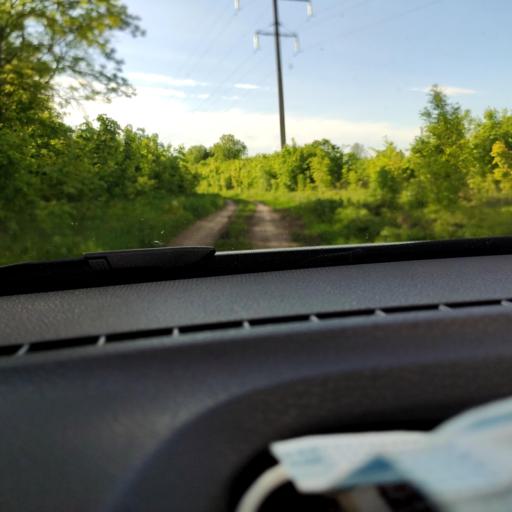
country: RU
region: Voronezj
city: Ramon'
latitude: 51.9473
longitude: 39.3635
